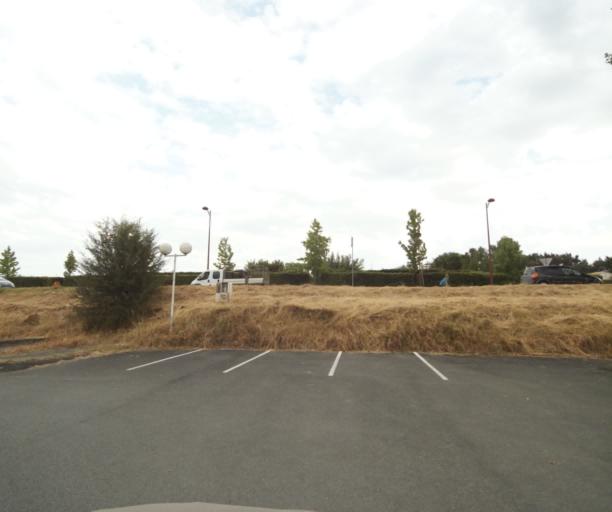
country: FR
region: Aquitaine
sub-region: Departement de la Gironde
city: Creon
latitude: 44.7718
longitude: -0.3414
